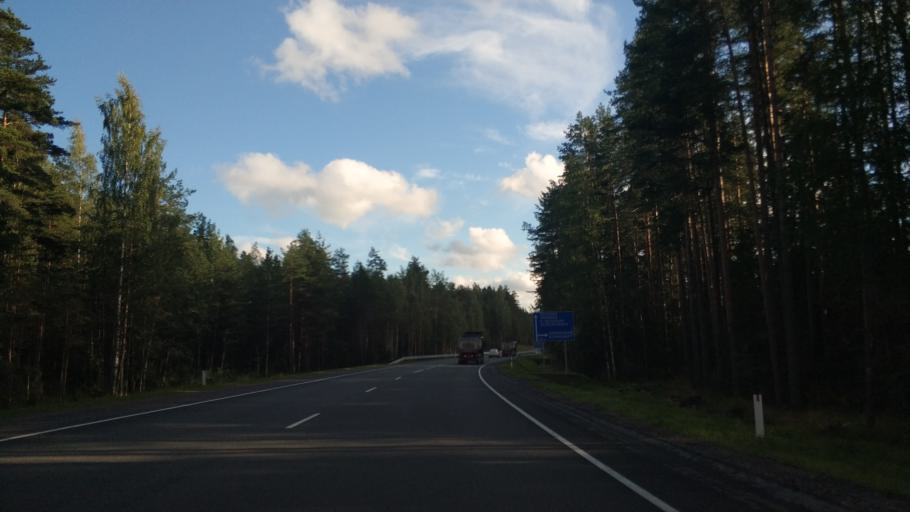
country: RU
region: Leningrad
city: Priozersk
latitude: 60.8754
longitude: 30.1623
